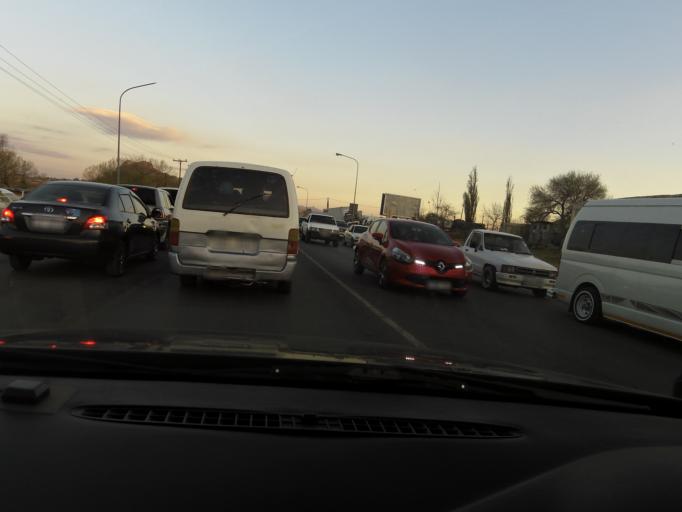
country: LS
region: Maseru
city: Maseru
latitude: -29.3355
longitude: 27.5098
